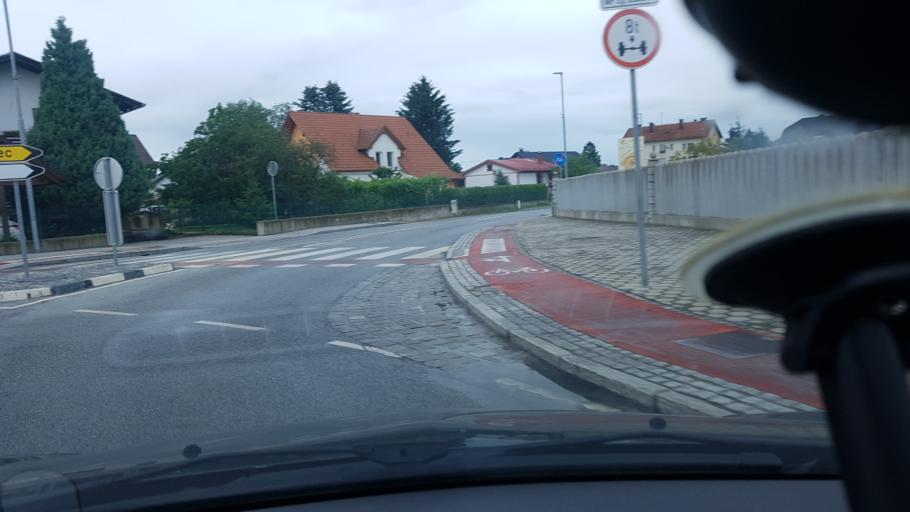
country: SI
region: Videm
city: Videm pri Ptuju
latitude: 46.3702
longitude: 15.8975
